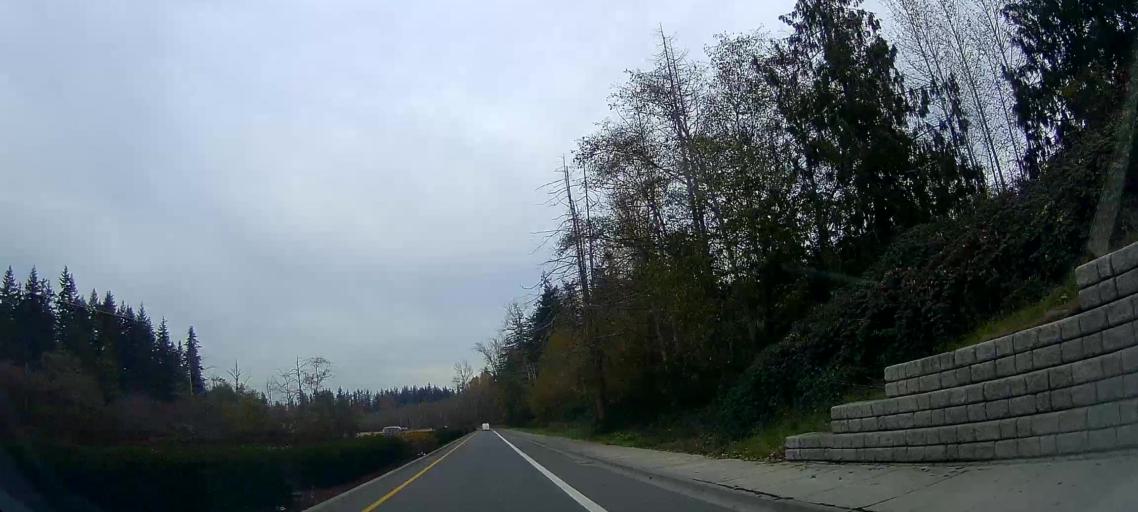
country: US
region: Washington
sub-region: Skagit County
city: Mount Vernon
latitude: 48.4022
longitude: -122.3159
